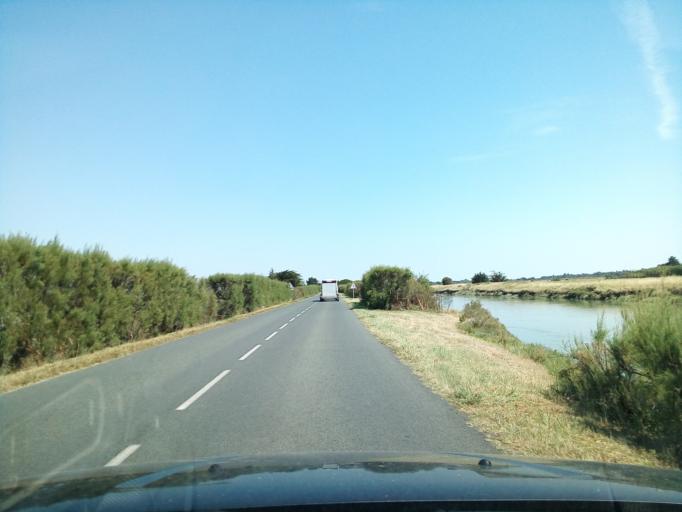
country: FR
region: Poitou-Charentes
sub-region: Departement de la Charente-Maritime
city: Boyard-Ville
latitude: 45.9679
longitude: -1.2648
